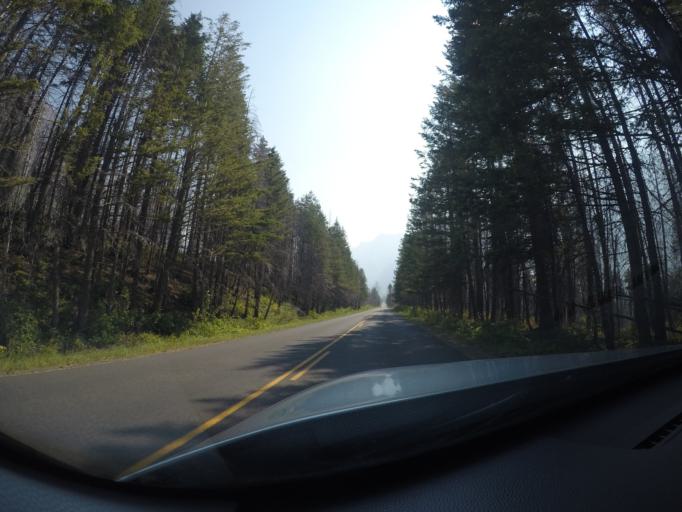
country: CA
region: Alberta
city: Cardston
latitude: 48.6749
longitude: -113.6216
